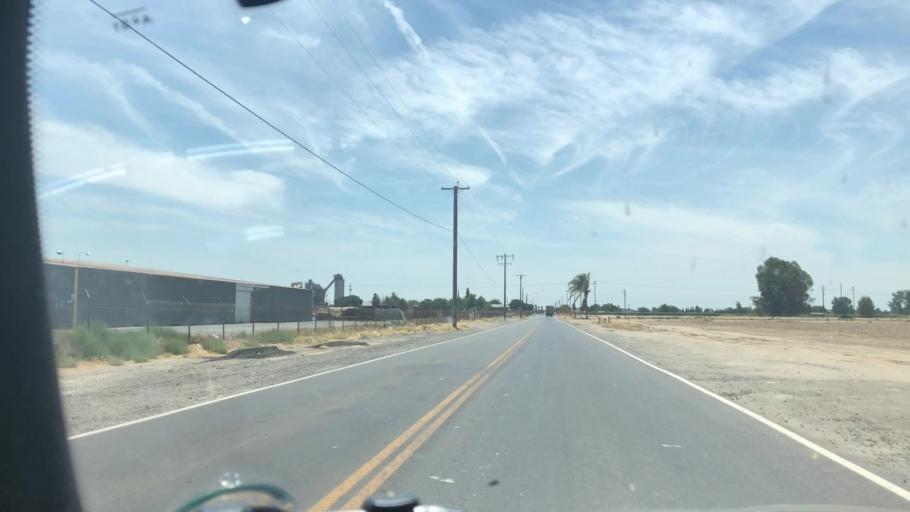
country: US
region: California
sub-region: Fresno County
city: Easton
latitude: 36.6812
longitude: -119.7547
